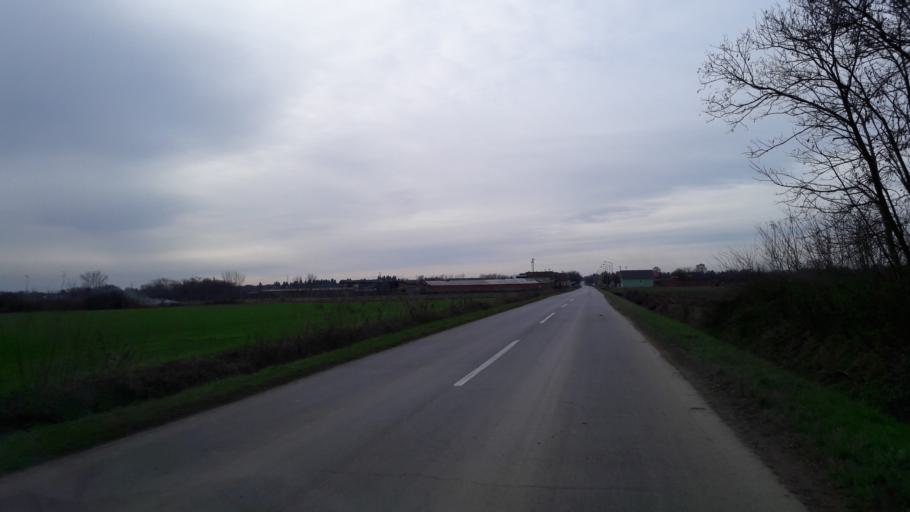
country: HR
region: Osjecko-Baranjska
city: Semeljci
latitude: 45.3701
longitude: 18.5504
